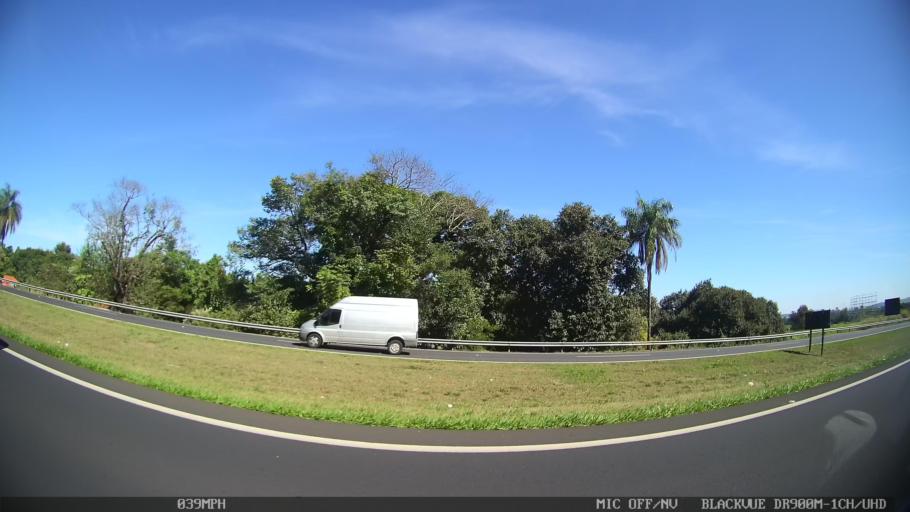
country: BR
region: Sao Paulo
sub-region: Santa Rita Do Passa Quatro
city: Santa Rita do Passa Quatro
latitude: -21.7485
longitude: -47.5726
